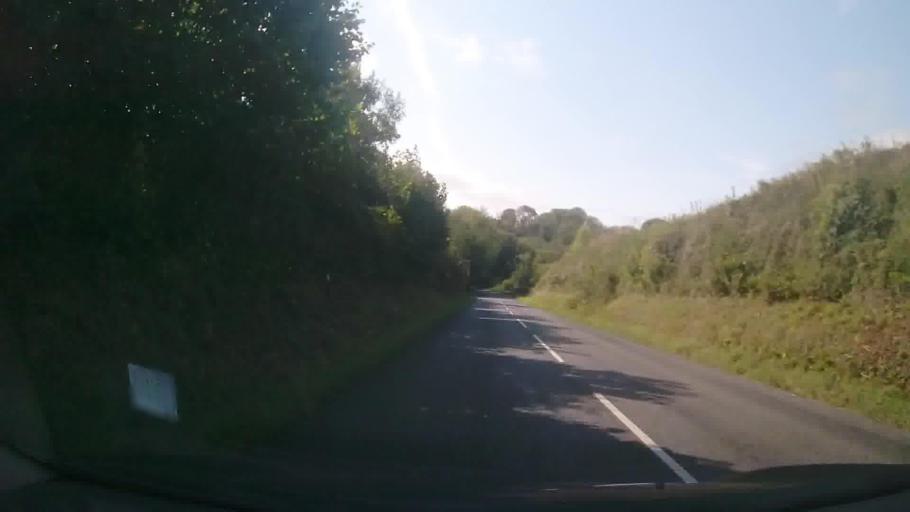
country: GB
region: Wales
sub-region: Pembrokeshire
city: Saundersfoot
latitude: 51.7381
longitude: -4.6882
